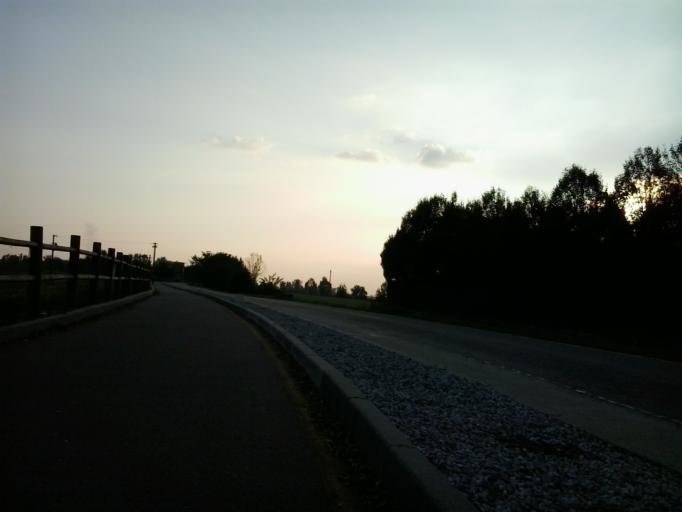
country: IT
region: Lombardy
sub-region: Provincia di Brescia
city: Azzano Mella
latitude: 45.4208
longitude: 10.1214
